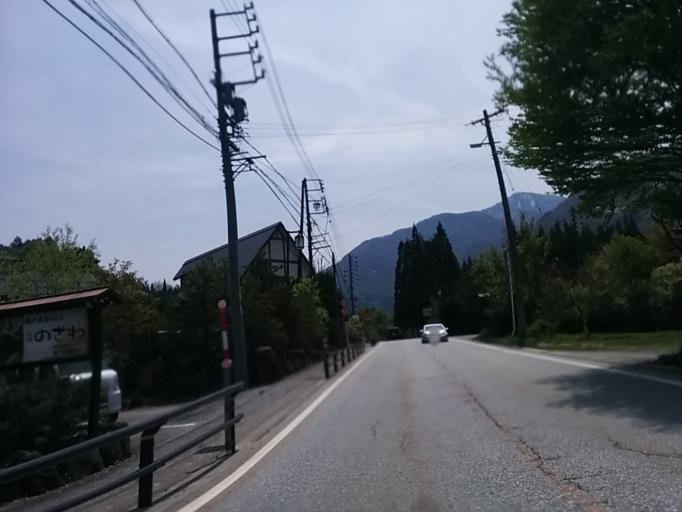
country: JP
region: Gifu
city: Takayama
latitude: 36.2378
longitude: 137.5288
